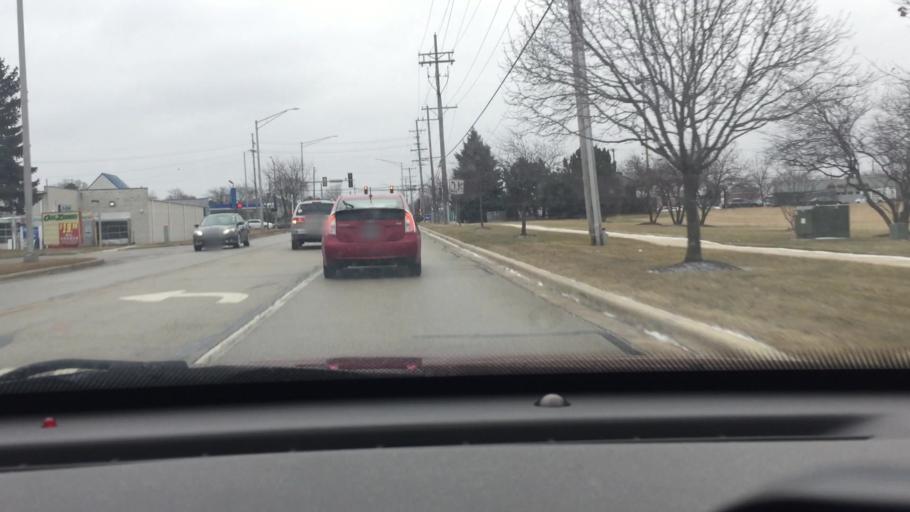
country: US
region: Illinois
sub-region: DuPage County
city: Naperville
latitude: 41.7818
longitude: -88.1804
